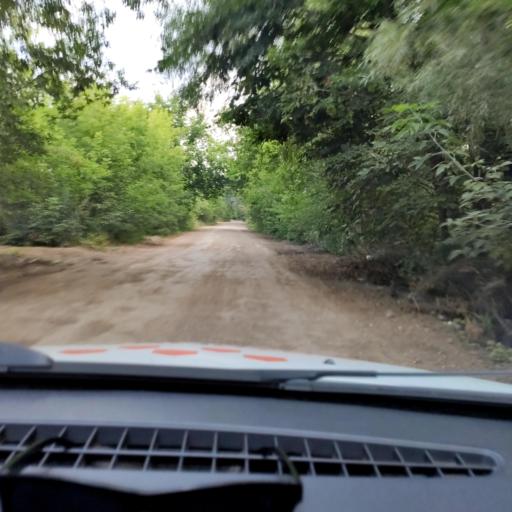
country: RU
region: Bashkortostan
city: Iglino
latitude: 54.7893
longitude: 56.1922
